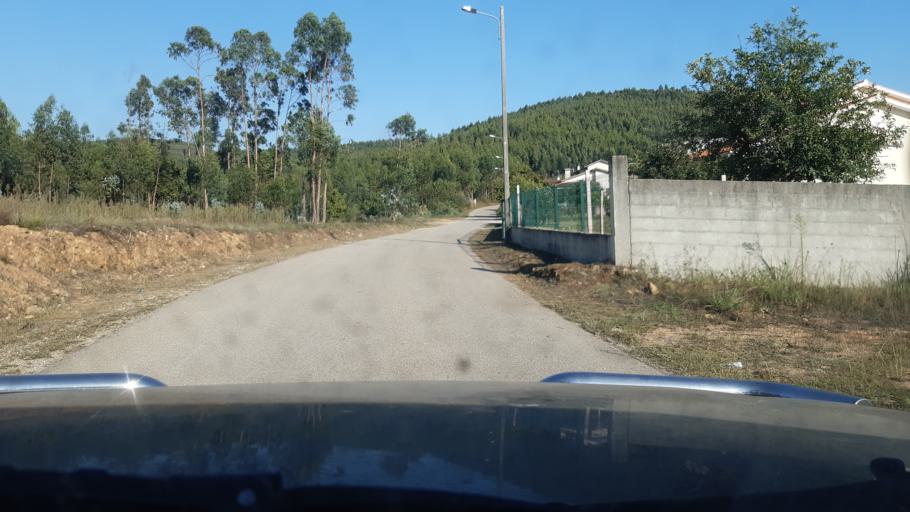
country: PT
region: Aveiro
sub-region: Agueda
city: Aguada de Cima
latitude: 40.5640
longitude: -8.3528
